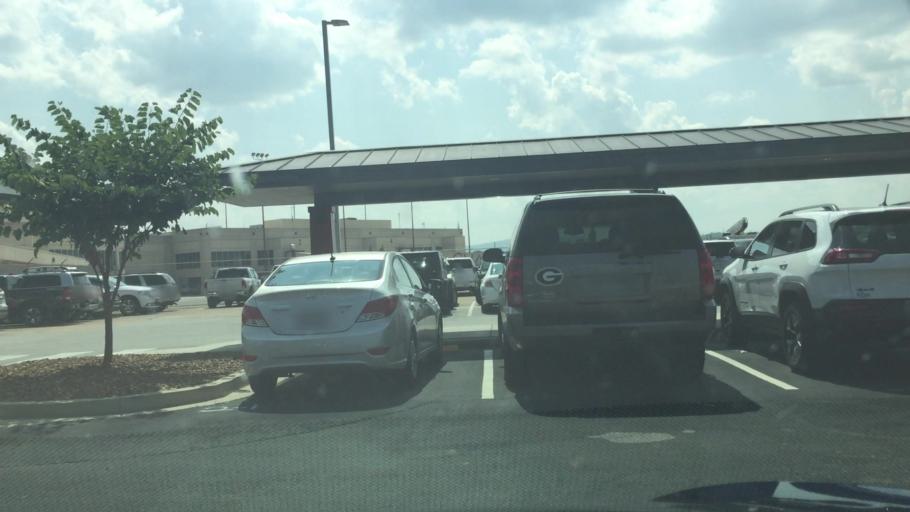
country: US
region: Tennessee
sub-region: Hamilton County
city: East Chattanooga
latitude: 35.0385
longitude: -85.1961
